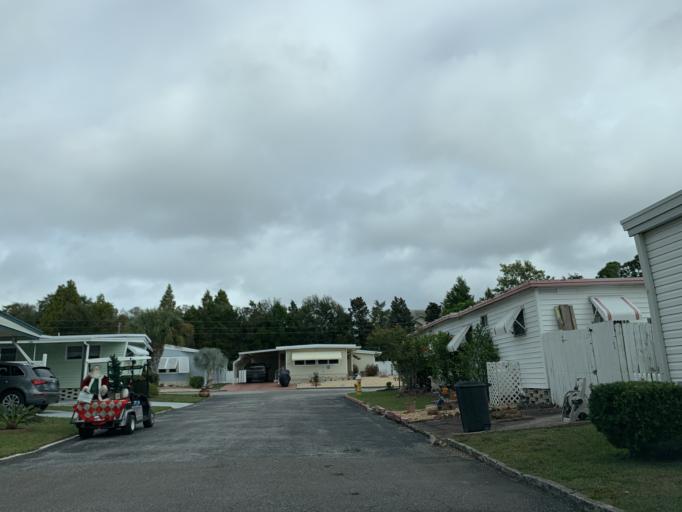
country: US
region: Florida
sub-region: Pinellas County
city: South Highpoint
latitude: 27.9525
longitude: -82.7286
